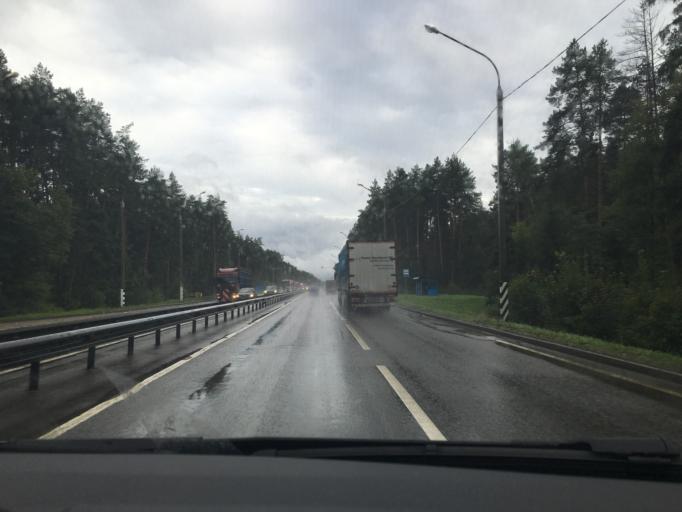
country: RU
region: Kaluga
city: Obninsk
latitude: 55.0634
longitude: 36.6219
